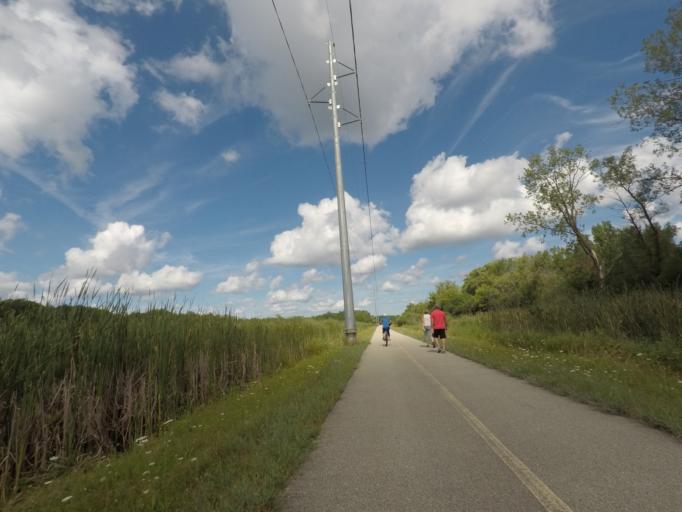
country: US
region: Wisconsin
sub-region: Waukesha County
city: Pewaukee
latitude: 43.0560
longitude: -88.2892
